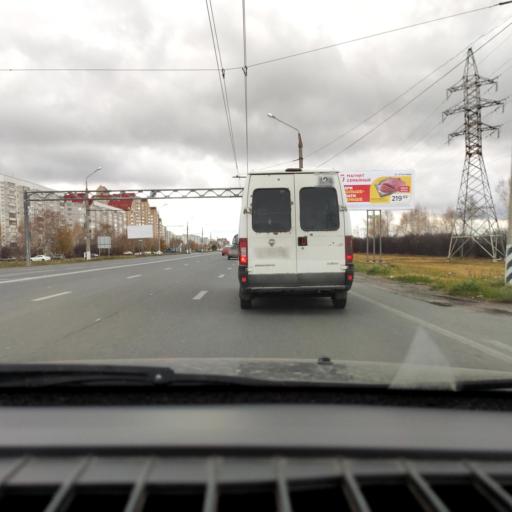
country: RU
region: Samara
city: Tol'yatti
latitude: 53.5460
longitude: 49.3726
